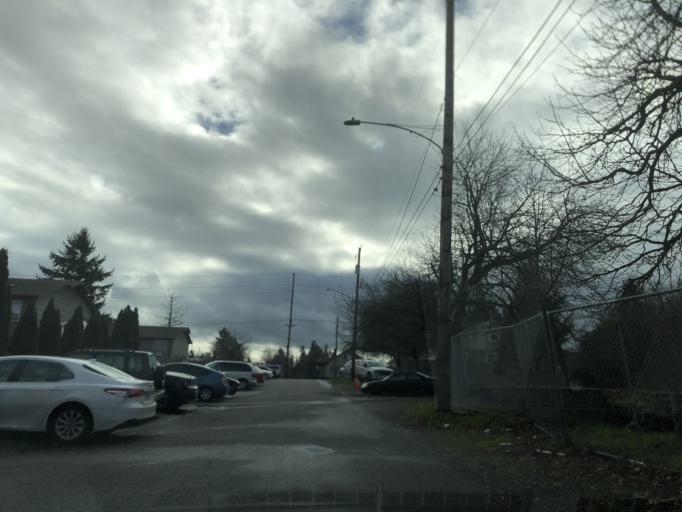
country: US
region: Washington
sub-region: Pierce County
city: Tacoma
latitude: 47.2292
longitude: -122.4553
